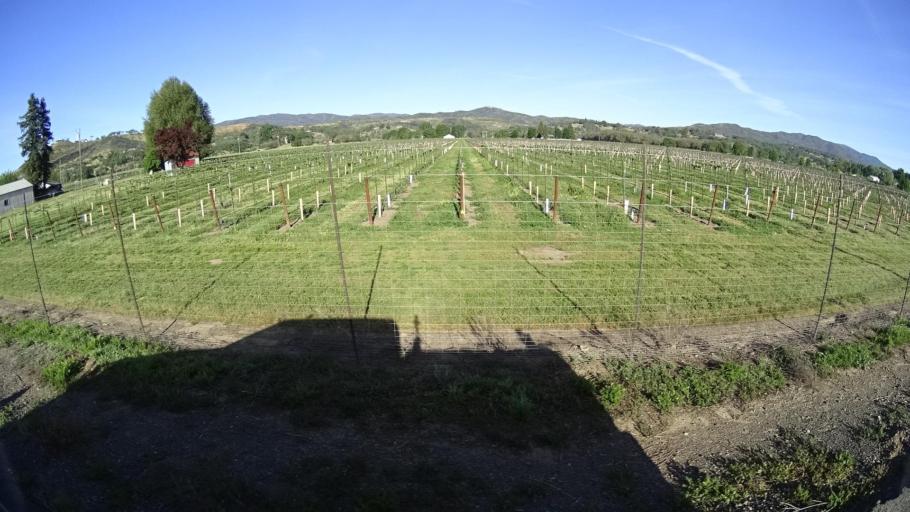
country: US
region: California
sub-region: Lake County
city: Lakeport
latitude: 39.0704
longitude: -122.9498
